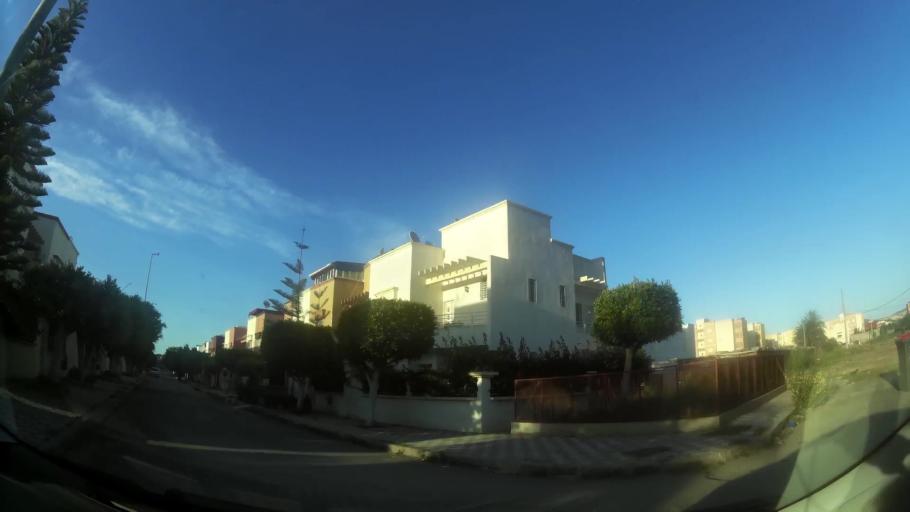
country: MA
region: Oriental
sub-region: Berkane-Taourirt
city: Madagh
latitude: 35.0793
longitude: -2.2395
